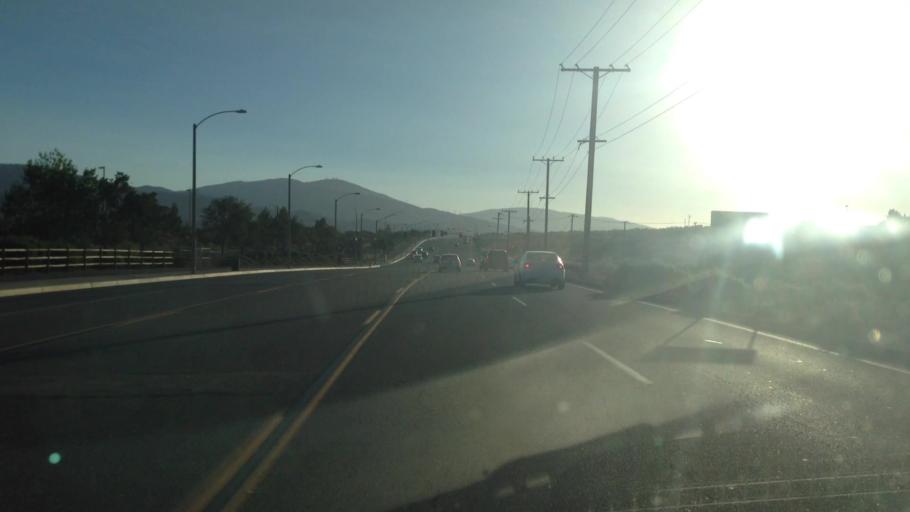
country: US
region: California
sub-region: Los Angeles County
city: Palmdale
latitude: 34.5580
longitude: -118.1180
